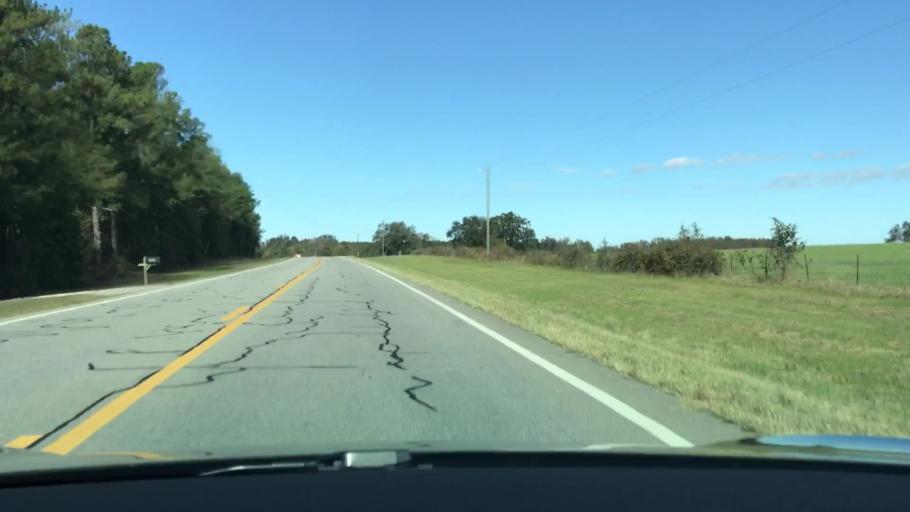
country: US
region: Georgia
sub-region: Warren County
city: Warrenton
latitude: 33.3412
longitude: -82.5746
